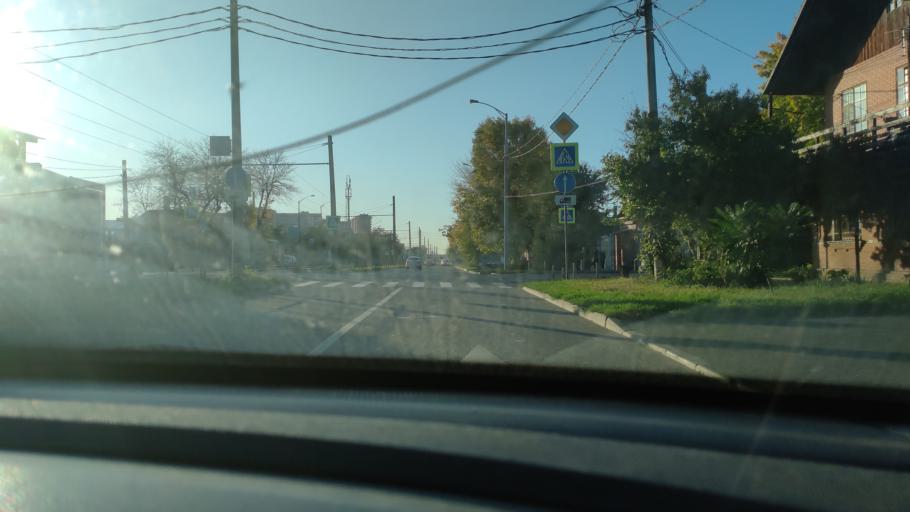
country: RU
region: Krasnodarskiy
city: Krasnodar
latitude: 45.0391
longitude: 38.9626
